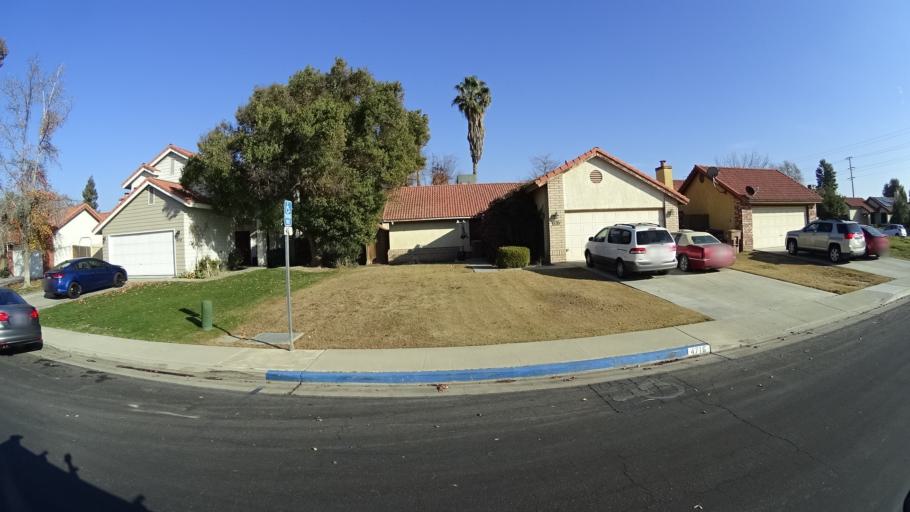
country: US
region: California
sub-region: Kern County
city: Greenacres
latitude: 35.3119
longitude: -119.0960
